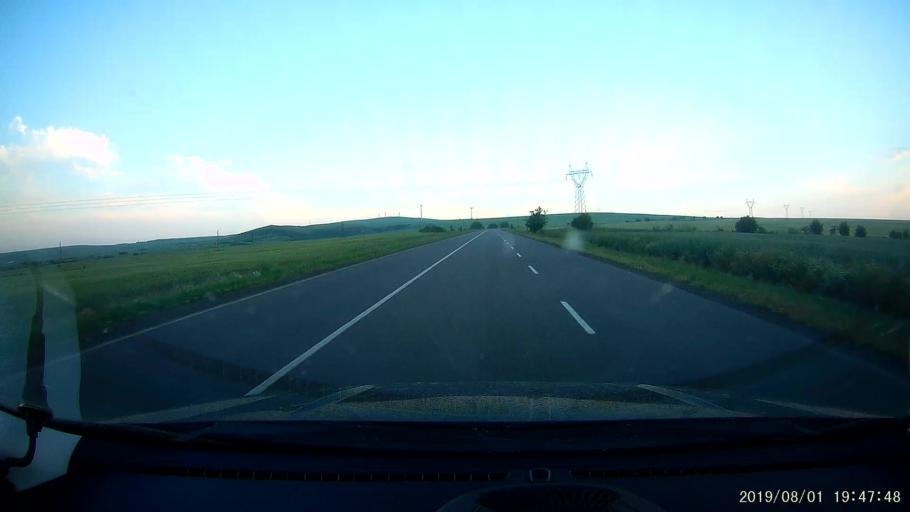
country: BG
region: Burgas
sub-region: Obshtina Karnobat
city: Karnobat
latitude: 42.6465
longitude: 26.9580
